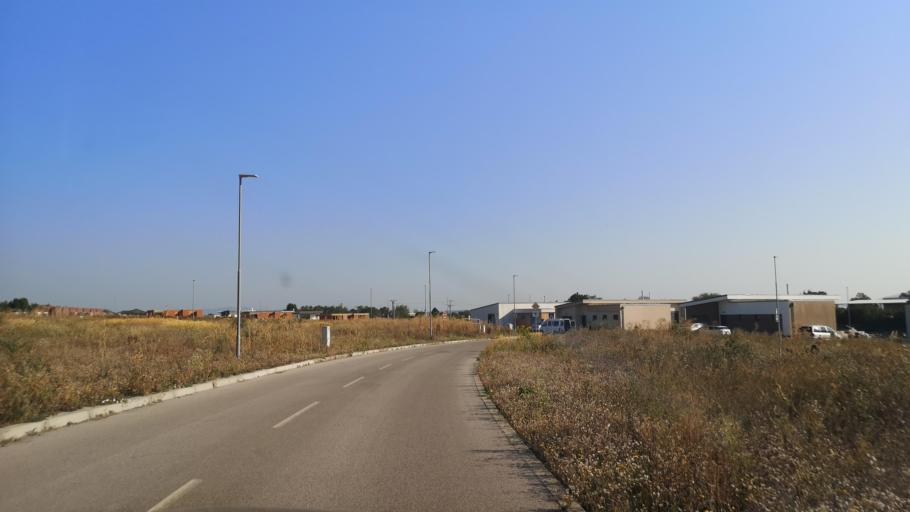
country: SK
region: Nitriansky
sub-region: Okres Nitra
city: Nitra
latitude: 48.3412
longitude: 18.0231
